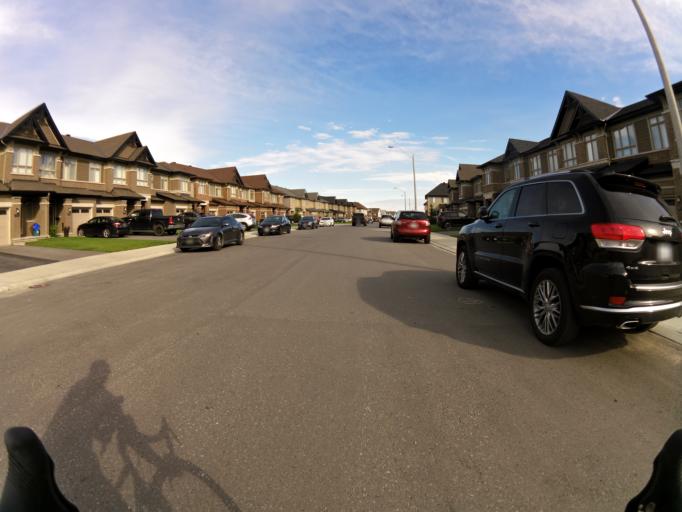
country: CA
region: Ontario
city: Bells Corners
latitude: 45.2708
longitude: -75.7801
